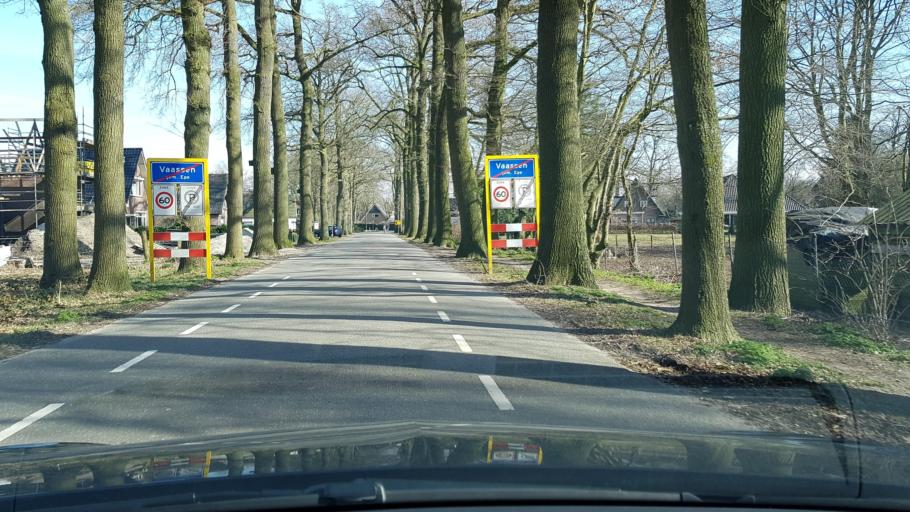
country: NL
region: Gelderland
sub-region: Gemeente Epe
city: Vaassen
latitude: 52.2933
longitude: 5.9669
